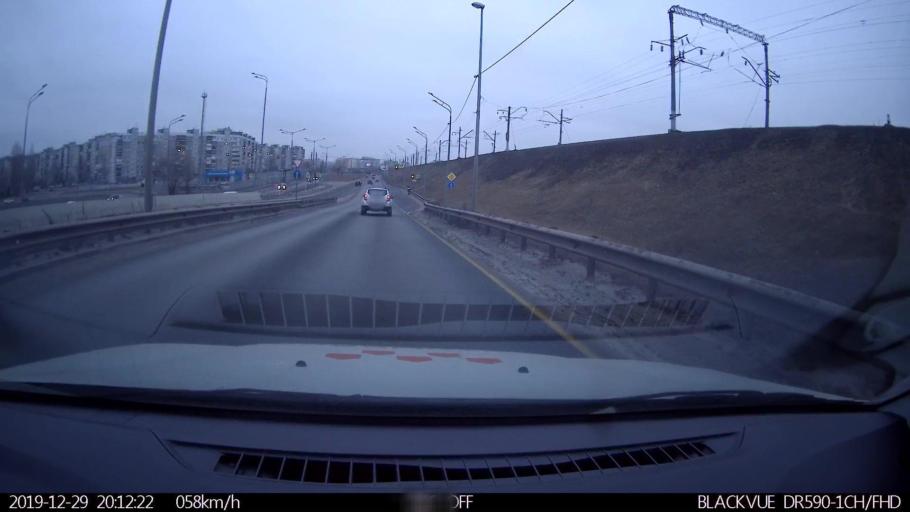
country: RU
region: Nizjnij Novgorod
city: Nizhniy Novgorod
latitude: 56.3471
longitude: 43.9213
